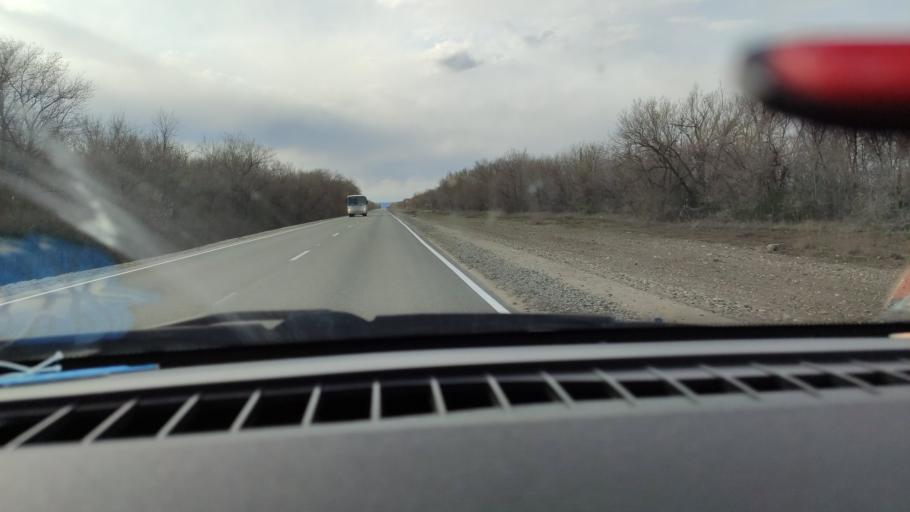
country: RU
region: Saratov
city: Privolzhskiy
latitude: 51.1680
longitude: 45.9430
